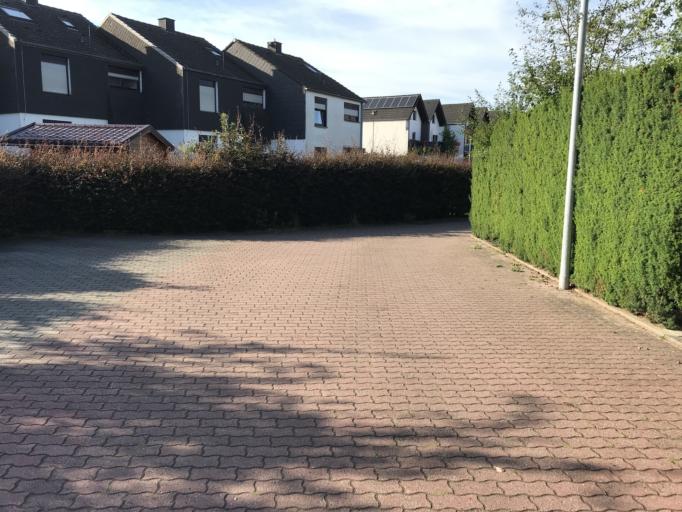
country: DE
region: North Rhine-Westphalia
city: Schwerte
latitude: 51.4411
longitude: 7.5442
